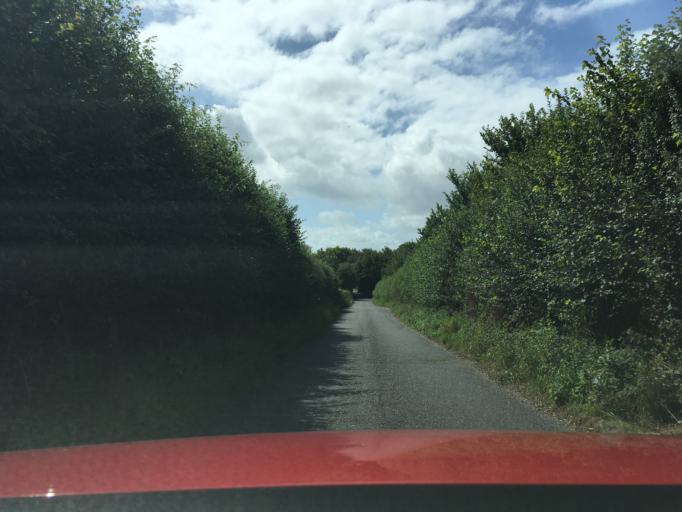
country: GB
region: England
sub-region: West Berkshire
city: Wickham
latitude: 51.4158
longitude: -1.4147
